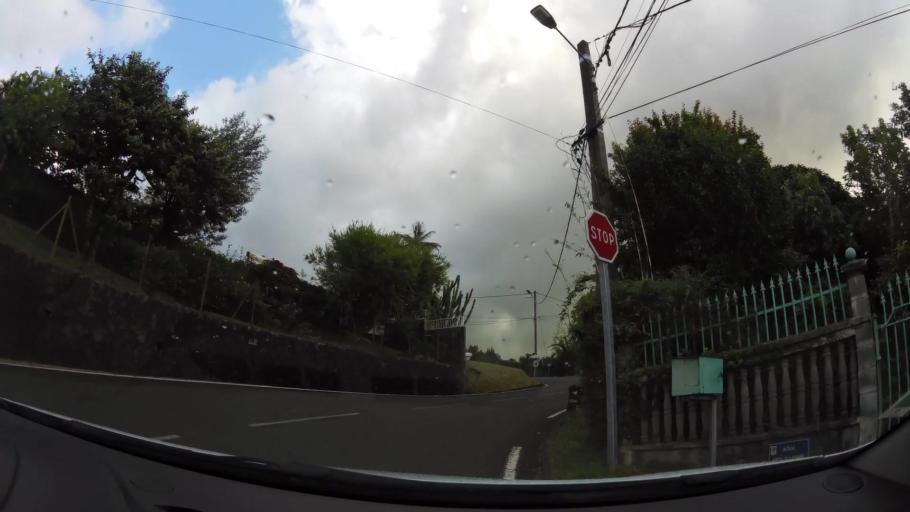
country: RE
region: Reunion
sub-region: Reunion
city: Saint-Denis
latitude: -20.9130
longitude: 55.4399
